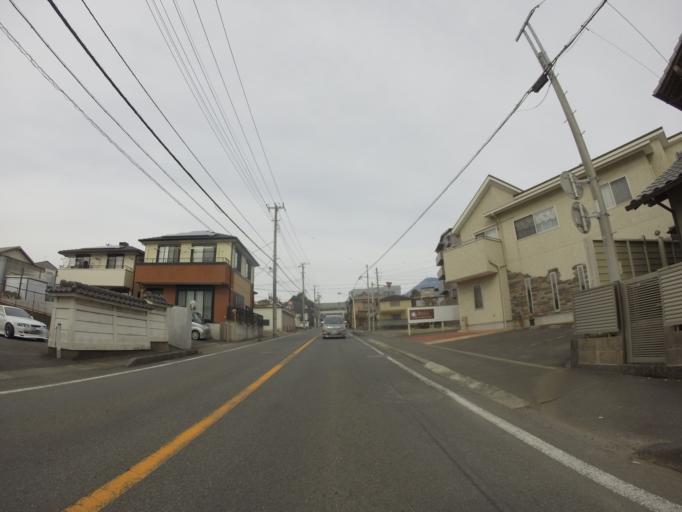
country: JP
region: Shizuoka
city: Fuji
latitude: 35.1791
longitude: 138.6822
